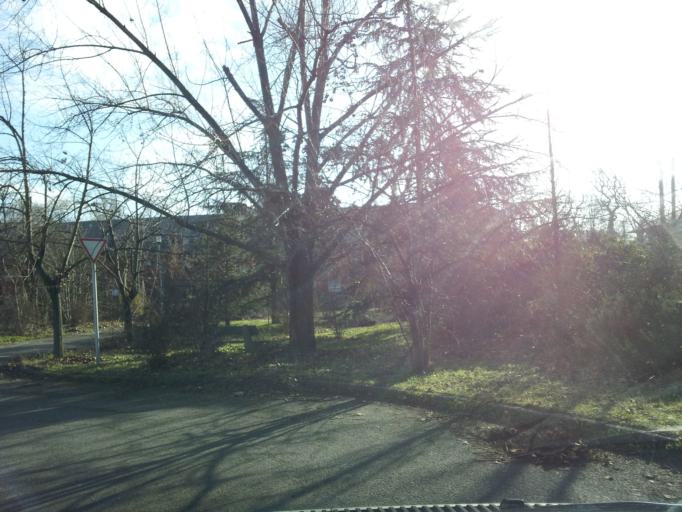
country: HU
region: Budapest
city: Budapest VIII. keruelet
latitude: 47.4735
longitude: 19.0938
